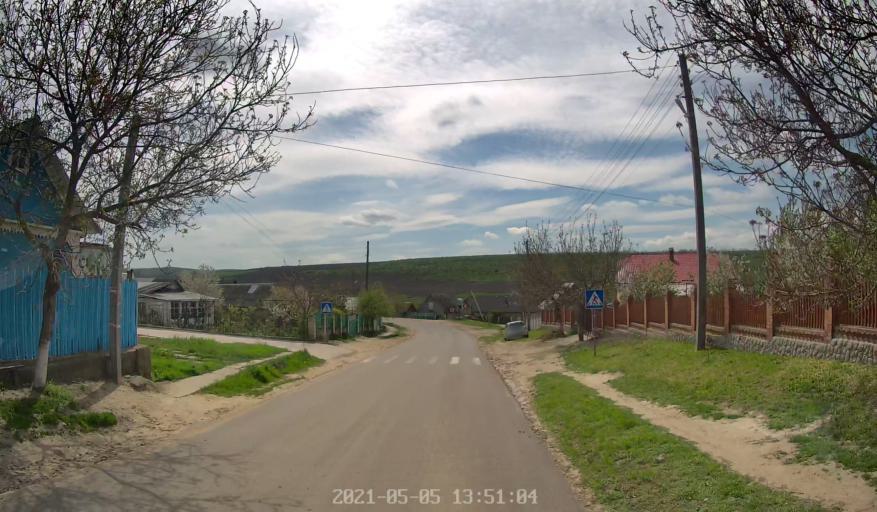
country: MD
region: Chisinau
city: Vadul lui Voda
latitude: 47.0649
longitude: 29.1314
